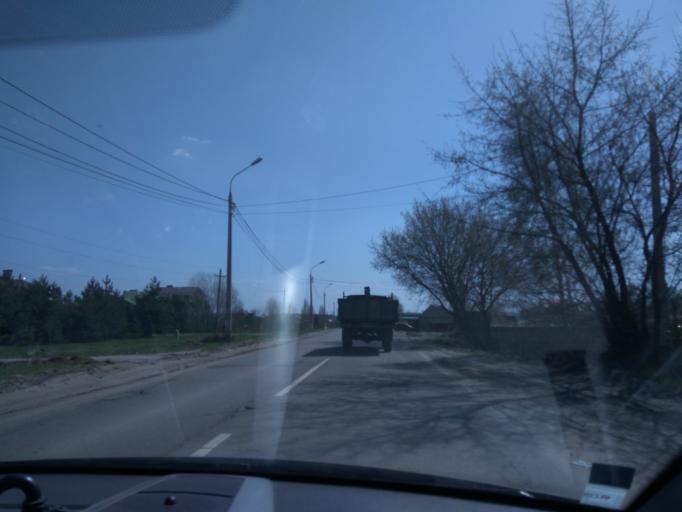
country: RU
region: Moskovskaya
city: Ramenskoye
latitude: 55.5828
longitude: 38.2604
